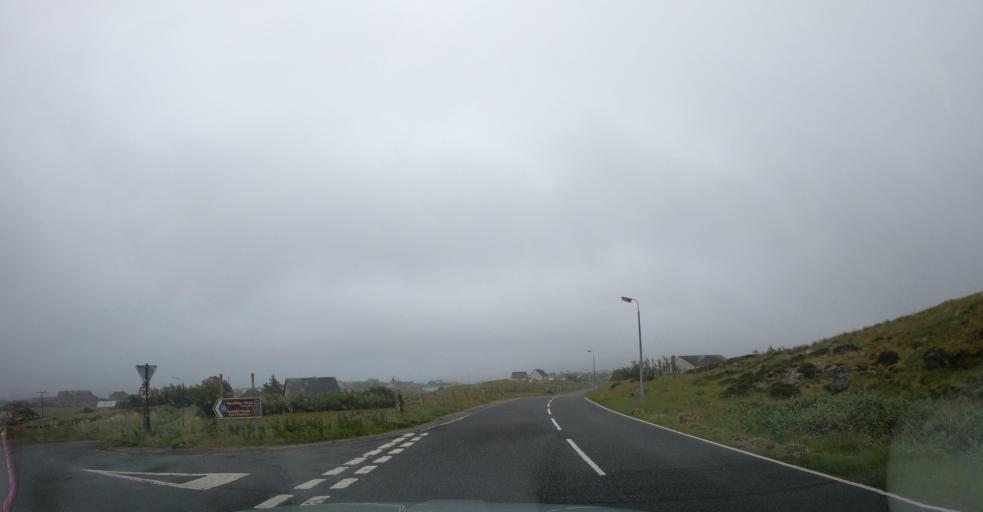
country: GB
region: Scotland
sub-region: Eilean Siar
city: Isle of North Uist
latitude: 57.6061
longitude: -7.1740
